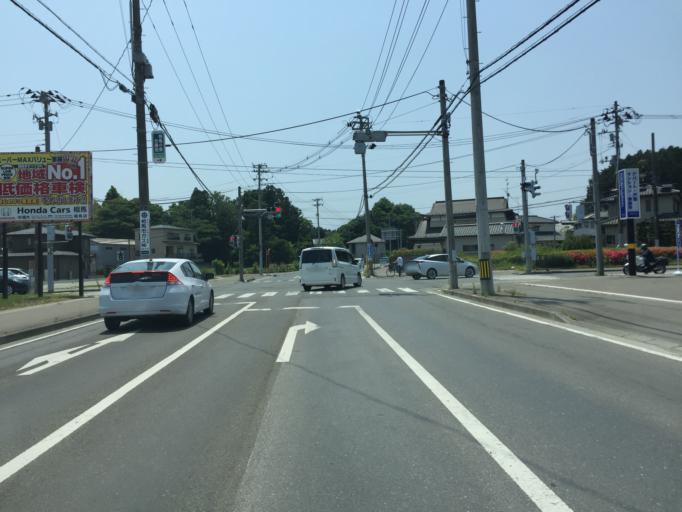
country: JP
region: Miyagi
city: Marumori
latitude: 37.8025
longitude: 140.9127
